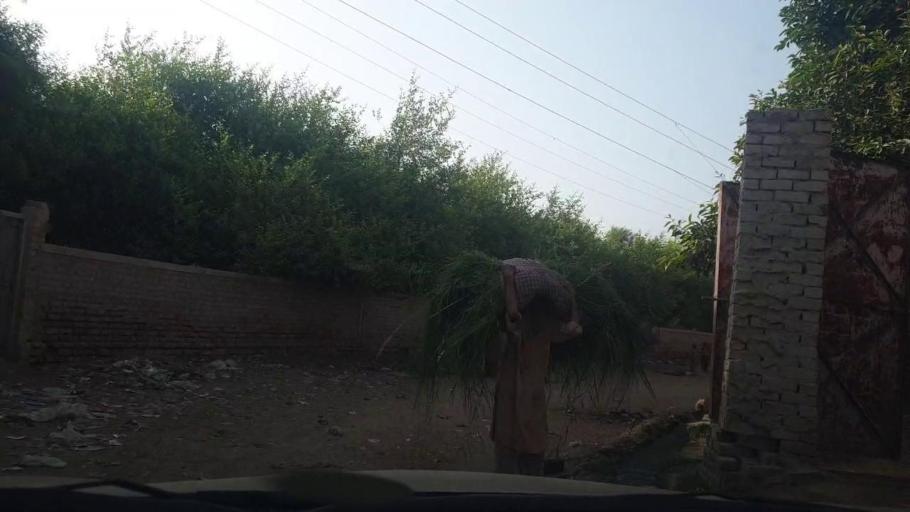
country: PK
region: Sindh
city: Larkana
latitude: 27.5798
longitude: 68.1778
